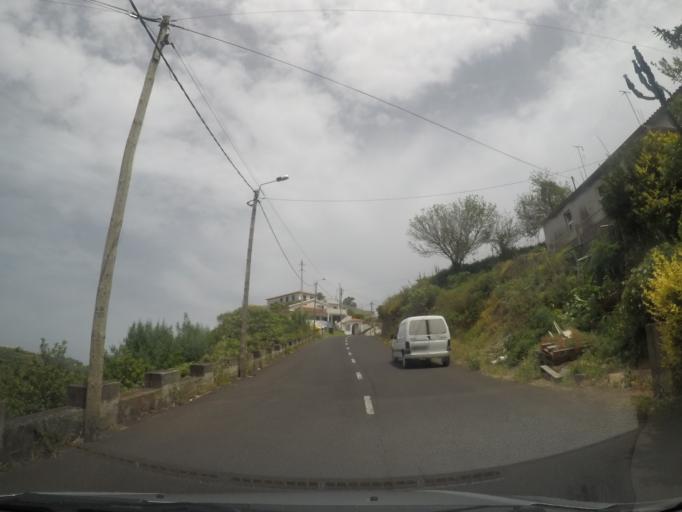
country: PT
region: Madeira
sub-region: Santa Cruz
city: Camacha
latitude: 32.6708
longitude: -16.8405
